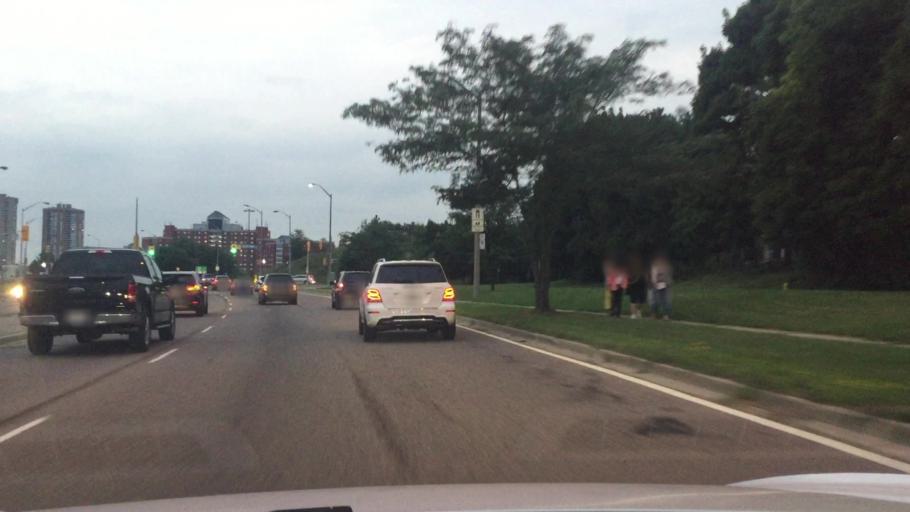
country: CA
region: Ontario
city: Willowdale
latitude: 43.7950
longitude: -79.3399
